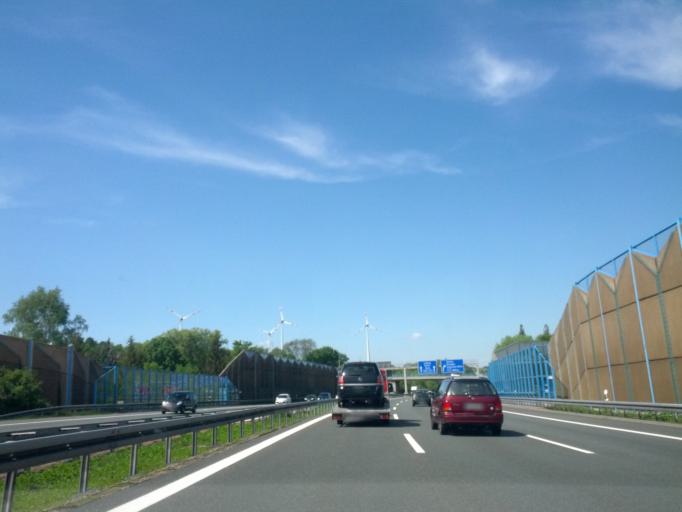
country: DE
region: Saxony
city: Wittgensdorf
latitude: 50.8322
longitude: 12.8467
